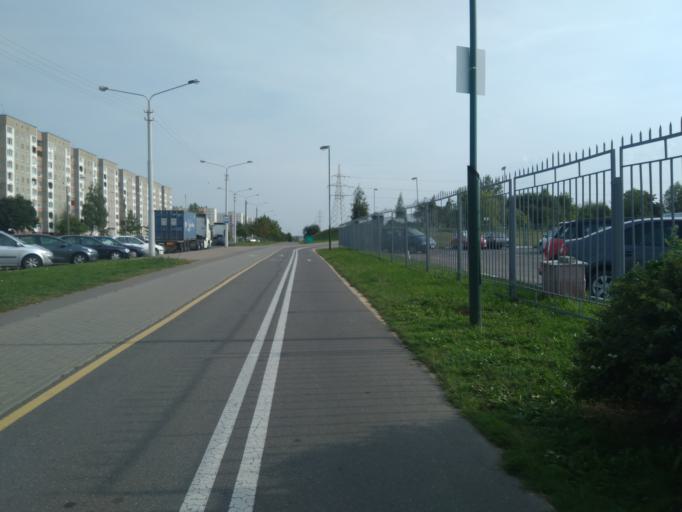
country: BY
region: Minsk
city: Minsk
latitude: 53.8616
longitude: 27.5876
